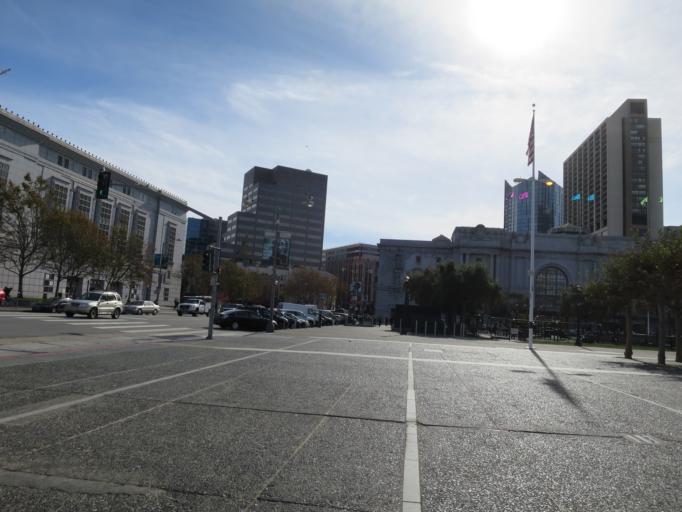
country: US
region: California
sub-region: San Francisco County
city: San Francisco
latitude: 37.7796
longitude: -122.4170
